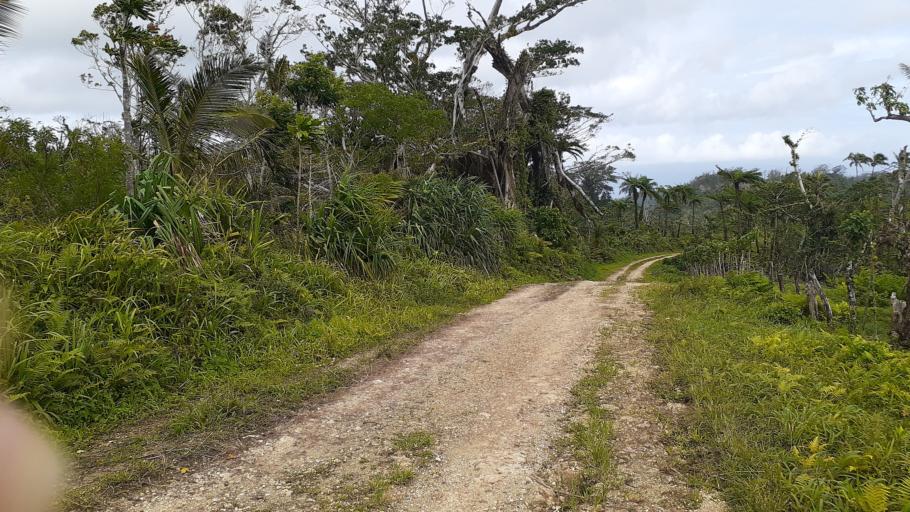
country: VU
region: Penama
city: Saratamata
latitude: -15.9579
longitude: 168.2247
